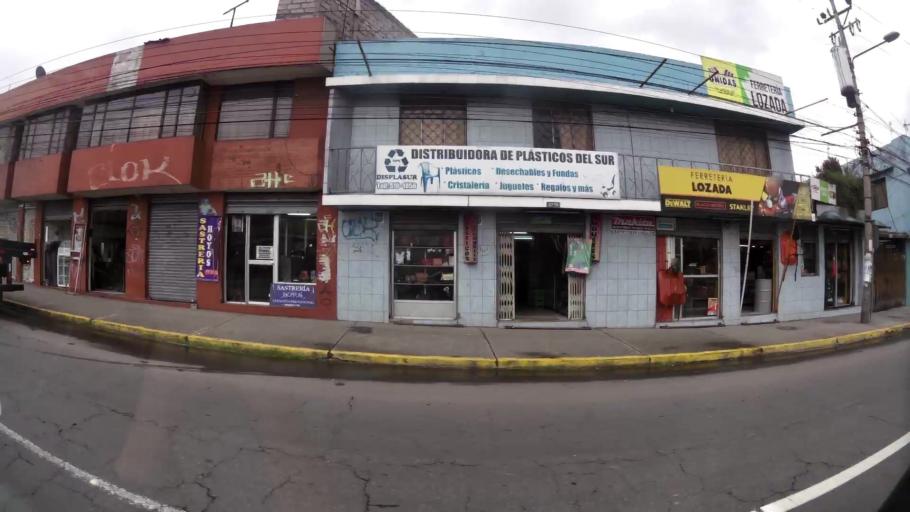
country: EC
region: Pichincha
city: Quito
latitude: -0.2750
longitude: -78.5526
